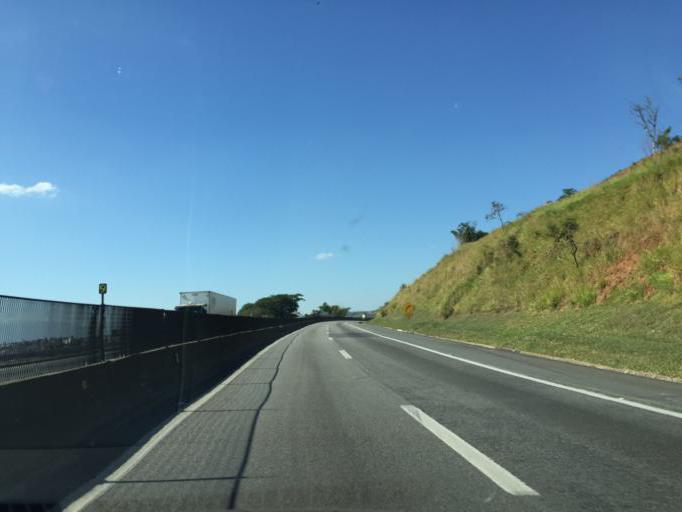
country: BR
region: Sao Paulo
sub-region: Guaratingueta
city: Guaratingueta
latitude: -22.8221
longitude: -45.2012
